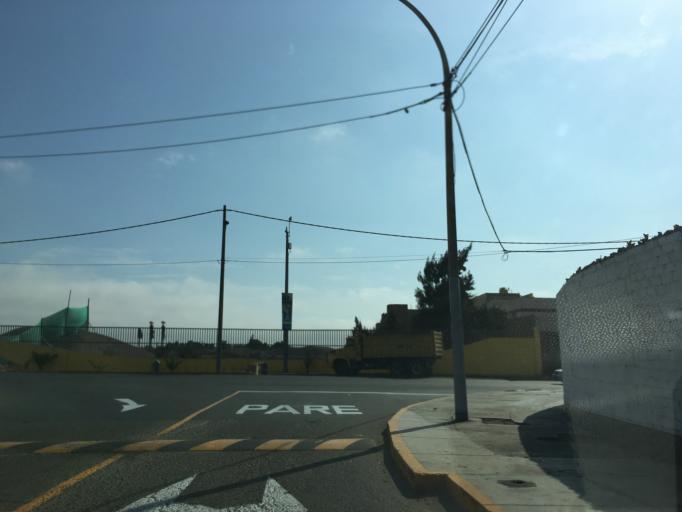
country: PE
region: Callao
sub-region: Callao
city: Callao
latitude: -12.0651
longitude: -77.0816
